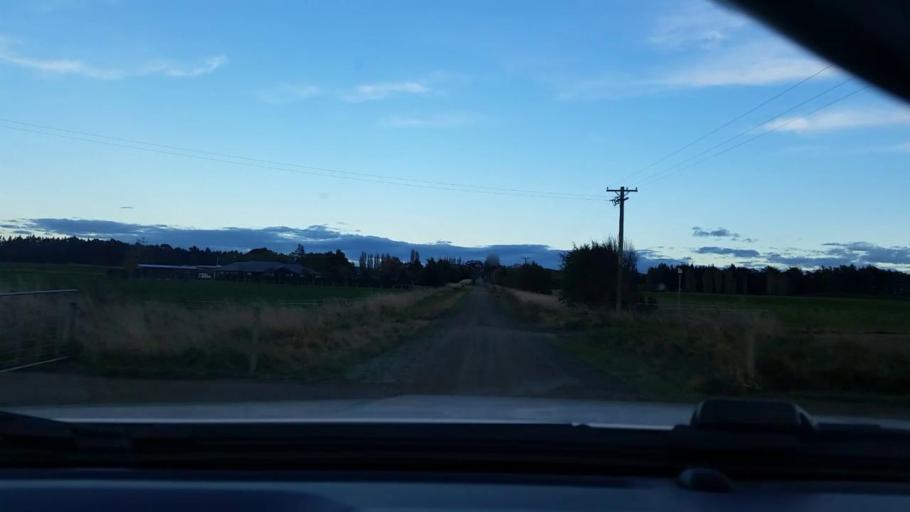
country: NZ
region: Southland
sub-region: Southland District
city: Winton
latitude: -46.1020
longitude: 168.4673
